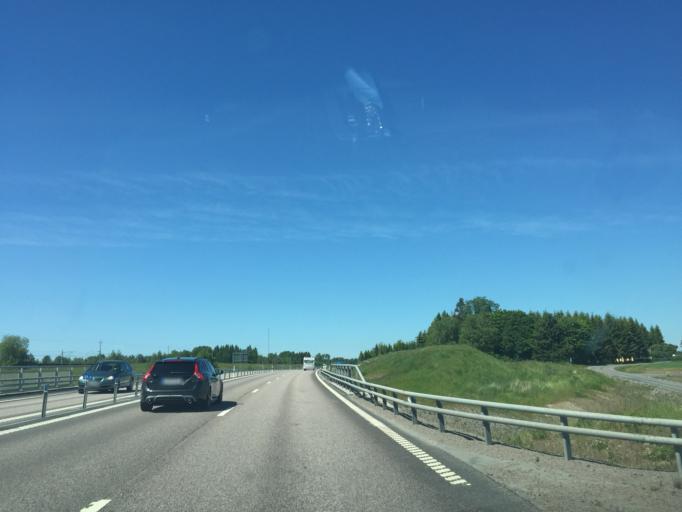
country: SE
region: OEstergoetland
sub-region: Motala Kommun
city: Stenstorp
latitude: 58.4080
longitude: 15.0826
